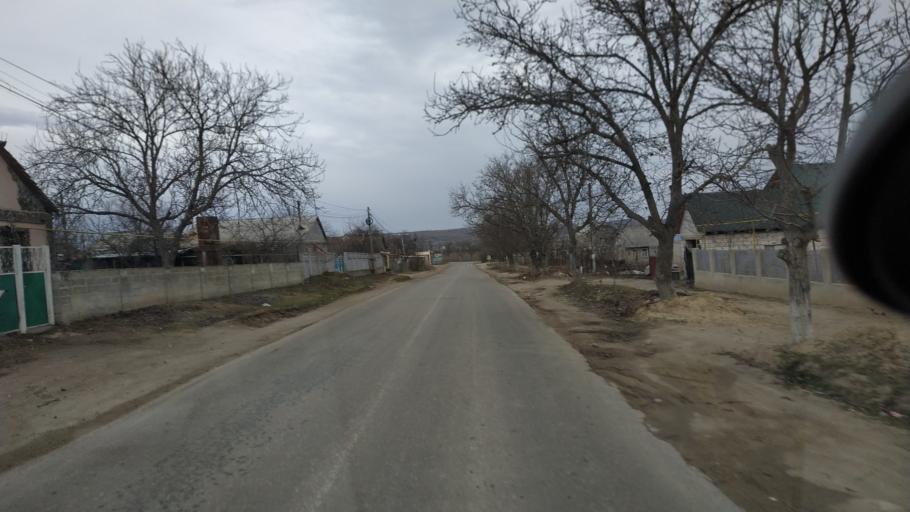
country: MD
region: Telenesti
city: Dubasari
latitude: 47.2465
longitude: 29.1395
